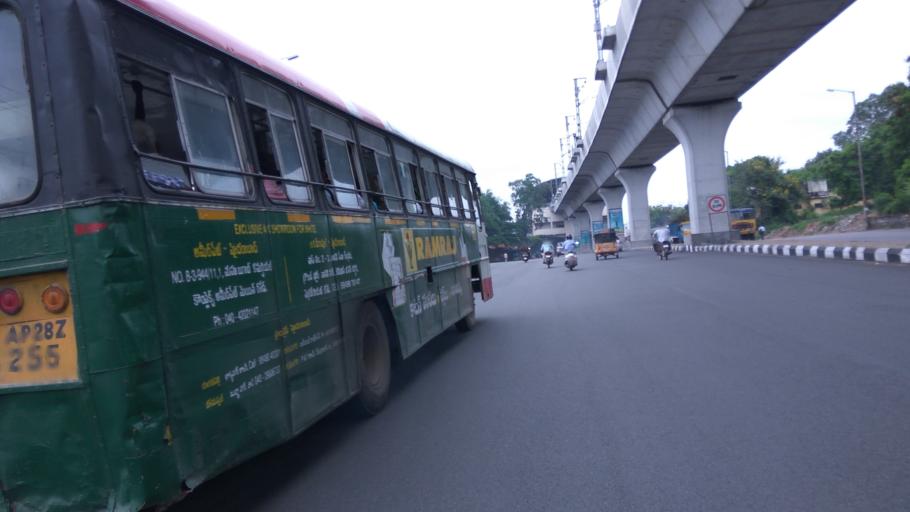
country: IN
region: Telangana
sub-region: Hyderabad
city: Malkajgiri
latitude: 17.4339
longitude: 78.5213
